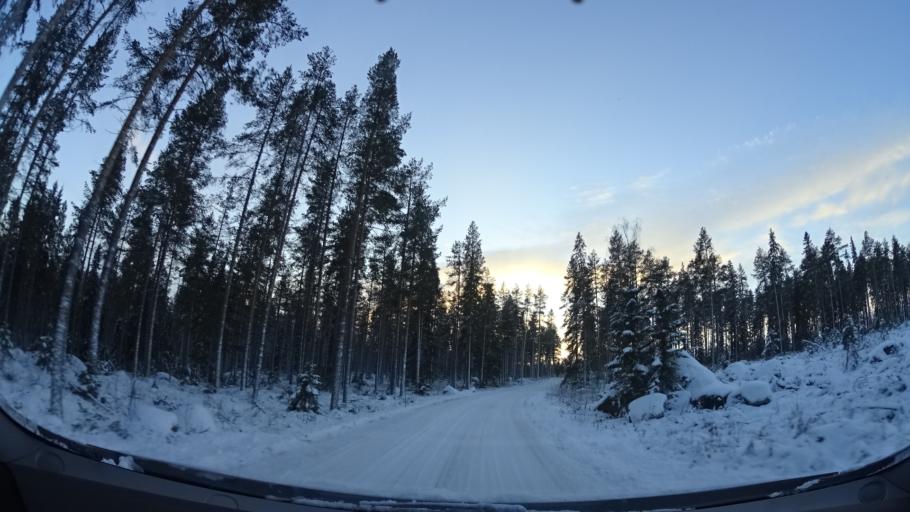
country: SE
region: Vaesterbotten
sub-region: Skelleftea Kommun
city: Kage
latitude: 64.8641
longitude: 21.0089
